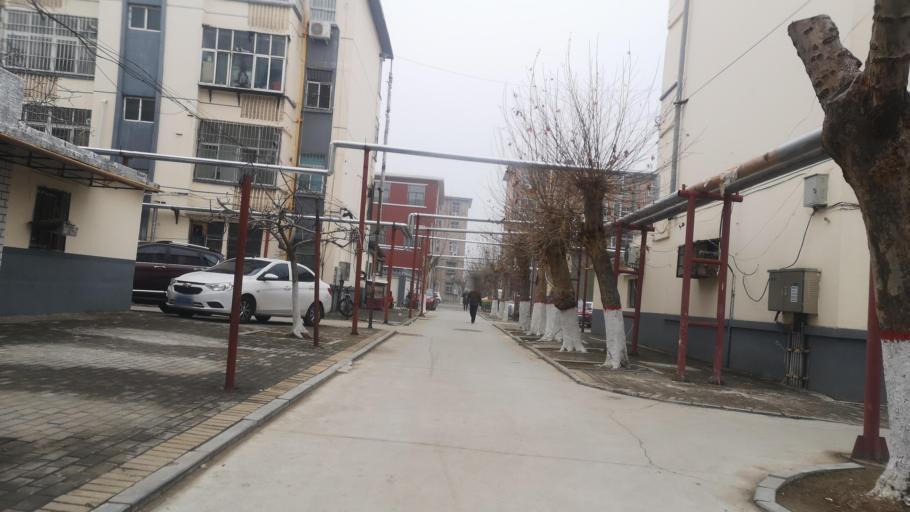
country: CN
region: Henan Sheng
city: Zhongyuanlu
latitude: 35.7645
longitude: 115.0716
